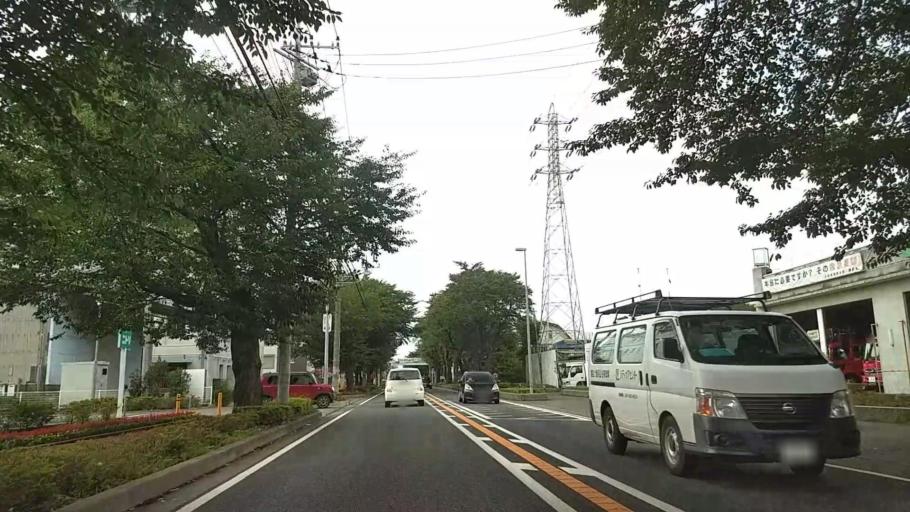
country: JP
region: Kanagawa
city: Minami-rinkan
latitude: 35.4385
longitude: 139.4670
